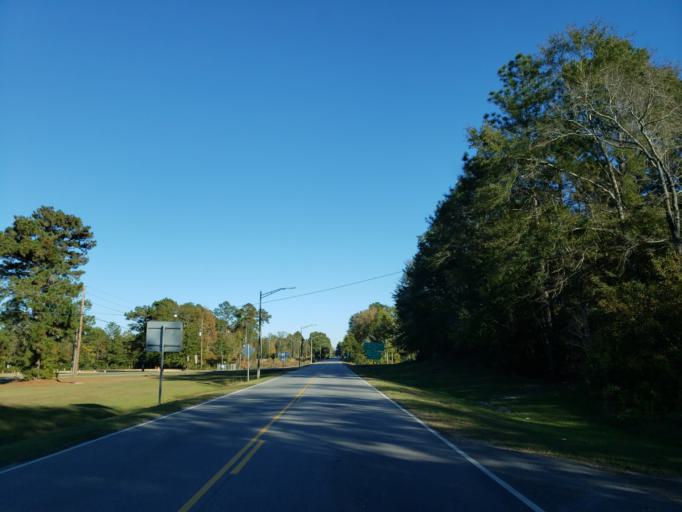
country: US
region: Mississippi
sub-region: Forrest County
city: Hattiesburg
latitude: 31.2666
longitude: -89.2828
